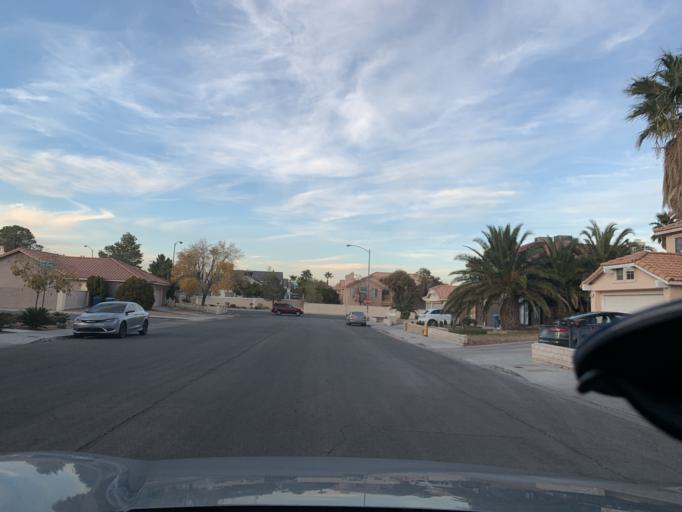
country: US
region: Nevada
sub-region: Clark County
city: Spring Valley
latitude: 36.0917
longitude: -115.2363
